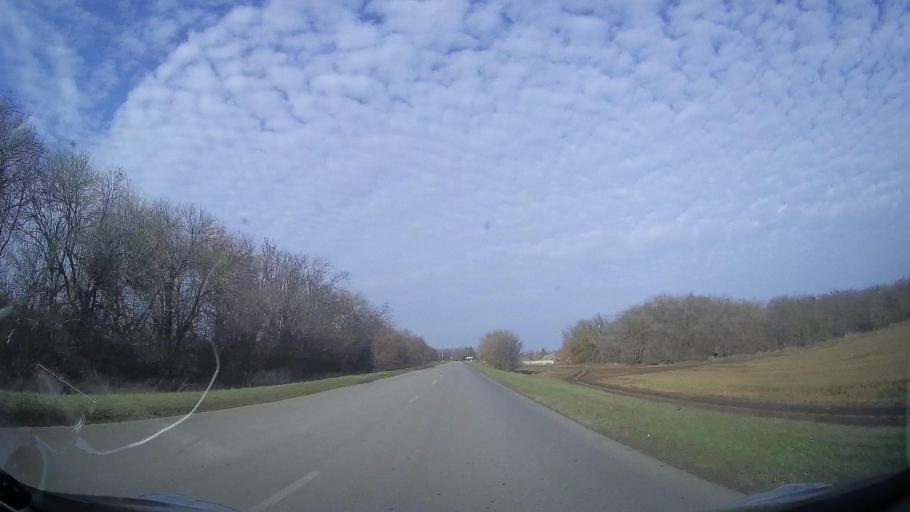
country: RU
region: Rostov
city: Gigant
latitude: 46.8324
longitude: 41.3354
